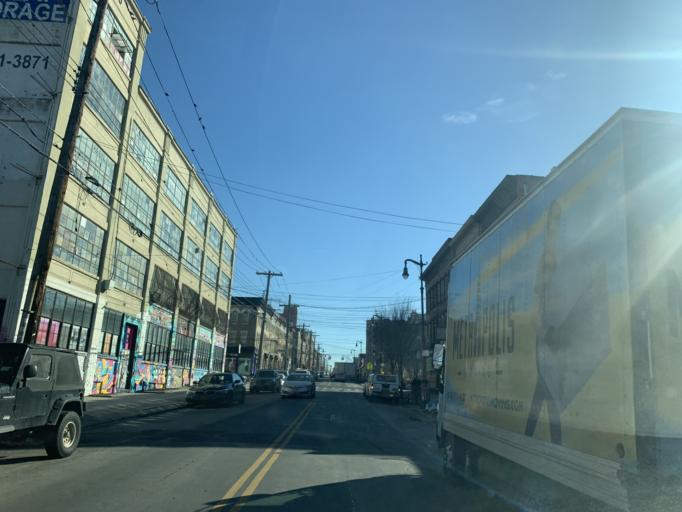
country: US
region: New York
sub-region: Queens County
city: Long Island City
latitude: 40.7060
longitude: -73.9220
